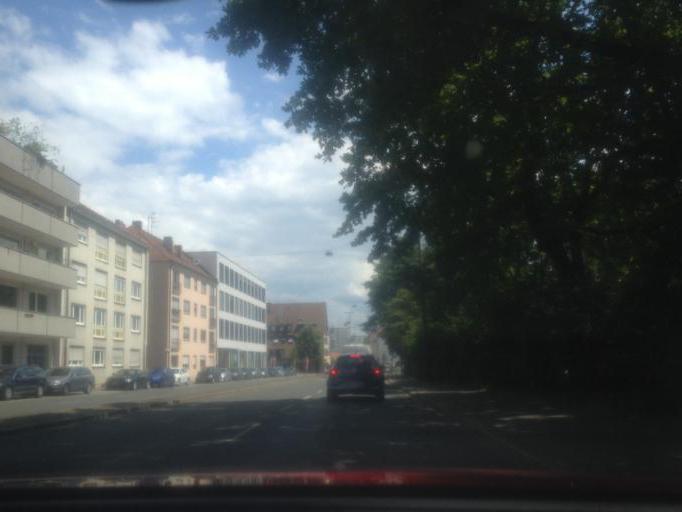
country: DE
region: Bavaria
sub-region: Regierungsbezirk Mittelfranken
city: Nuernberg
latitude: 49.4554
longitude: 11.0913
